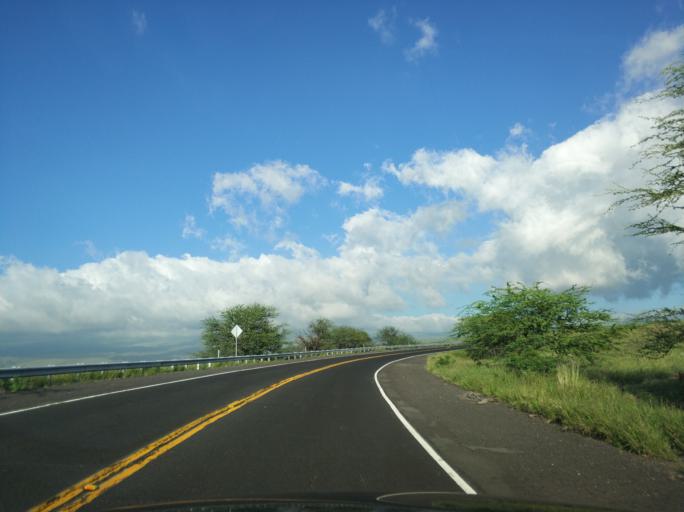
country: US
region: Hawaii
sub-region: Hawaii County
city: Waikoloa Village
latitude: 19.9758
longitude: -155.8257
